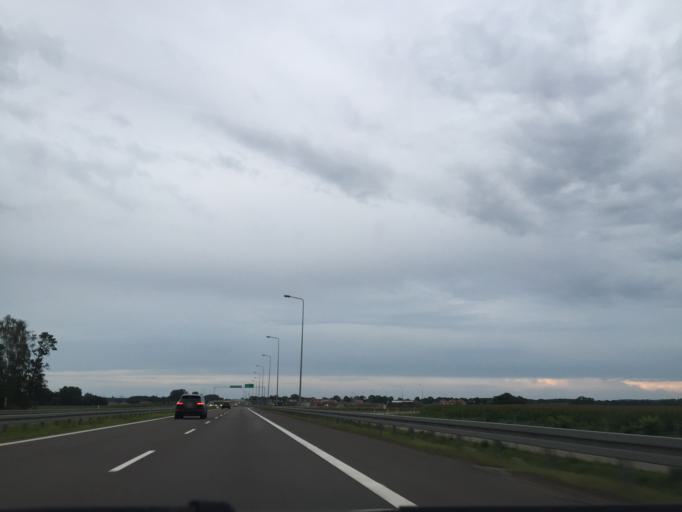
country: PL
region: Podlasie
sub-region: Powiat bialostocki
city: Tykocin
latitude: 53.1526
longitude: 22.8509
